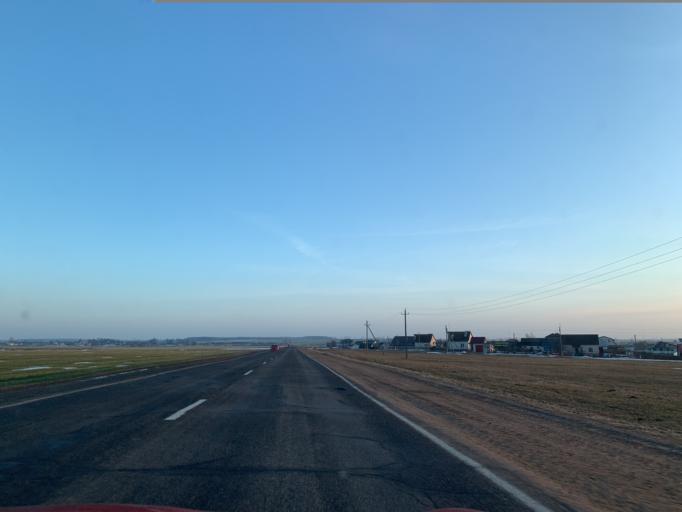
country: BY
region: Minsk
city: Haradzyeya
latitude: 53.3154
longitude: 26.5627
